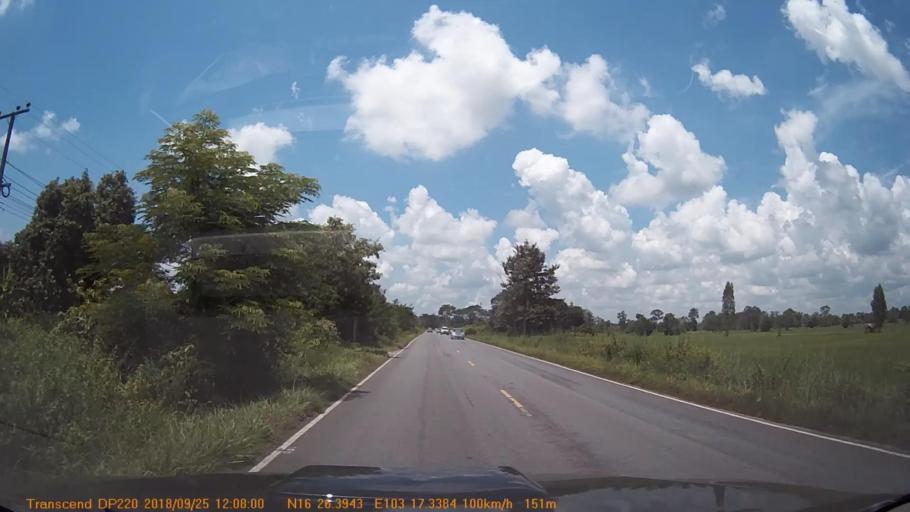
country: TH
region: Kalasin
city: Yang Talat
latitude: 16.4398
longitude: 103.2891
